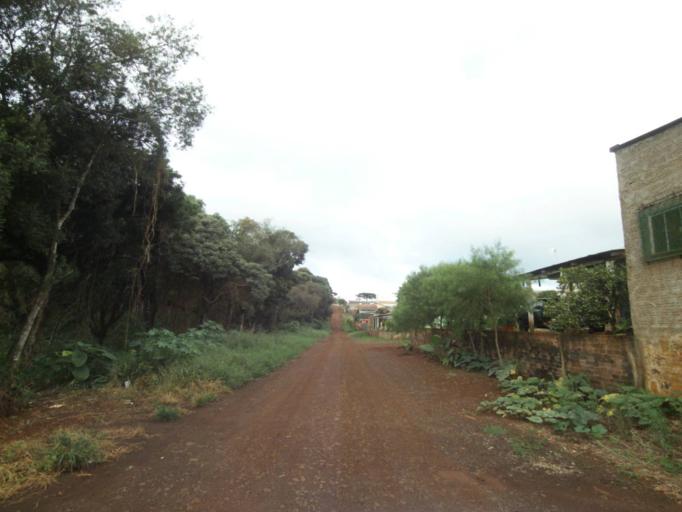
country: BR
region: Parana
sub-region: Pitanga
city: Pitanga
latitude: -24.9425
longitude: -51.8711
